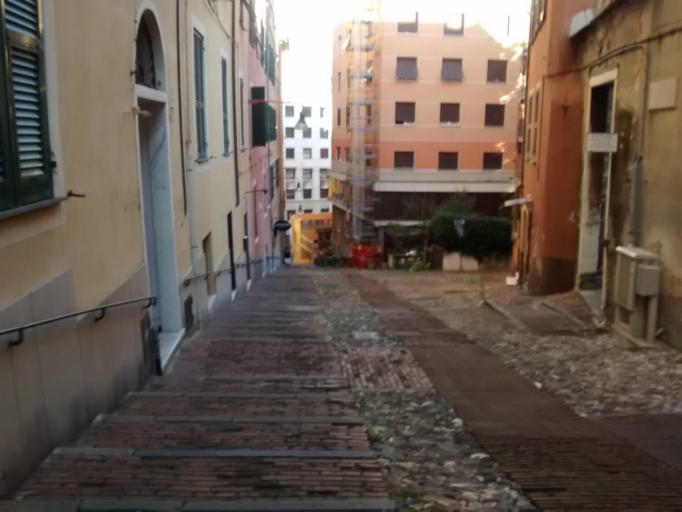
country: IT
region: Liguria
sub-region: Provincia di Genova
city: San Teodoro
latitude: 44.4041
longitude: 8.9371
